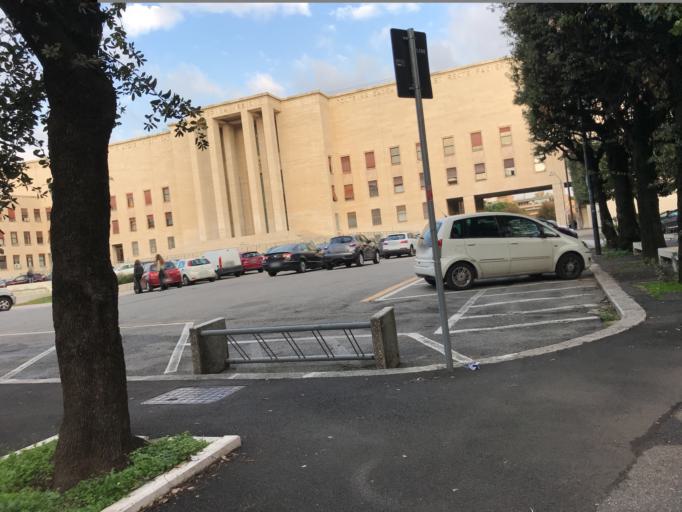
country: IT
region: Latium
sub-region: Citta metropolitana di Roma Capitale
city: Rome
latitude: 41.9024
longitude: 12.5144
